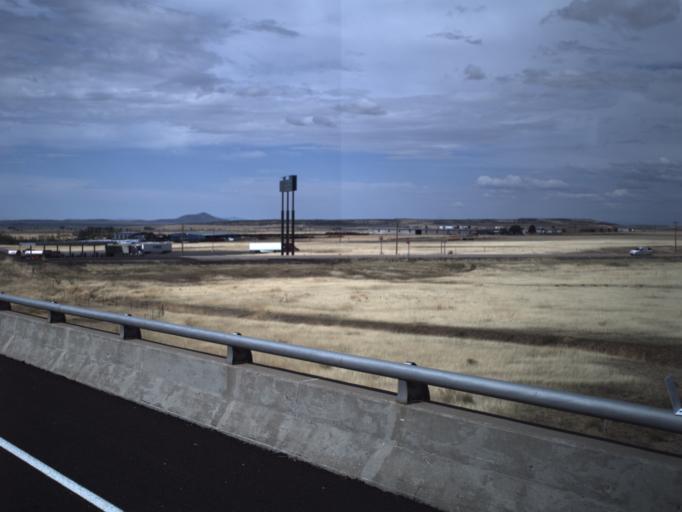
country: US
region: Utah
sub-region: Millard County
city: Fillmore
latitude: 38.9487
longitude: -112.3497
